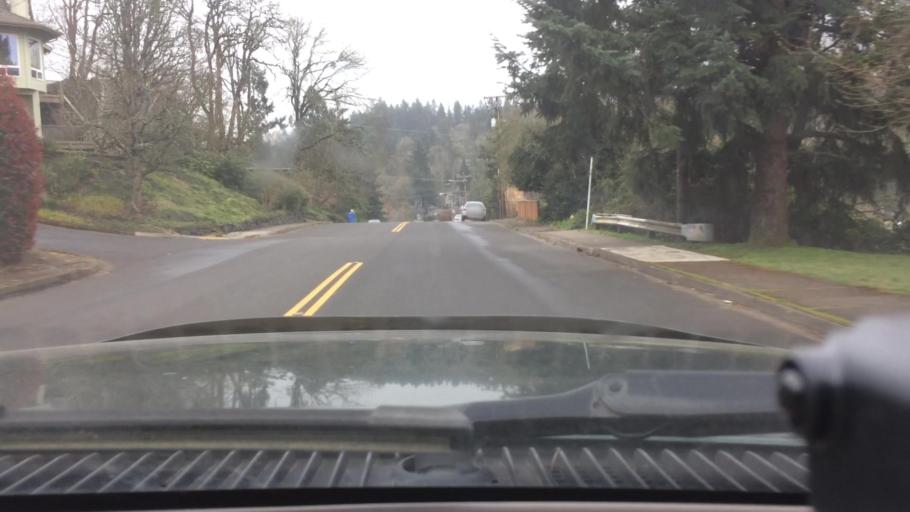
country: US
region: Oregon
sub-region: Lane County
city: Eugene
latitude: 44.0302
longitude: -123.1013
